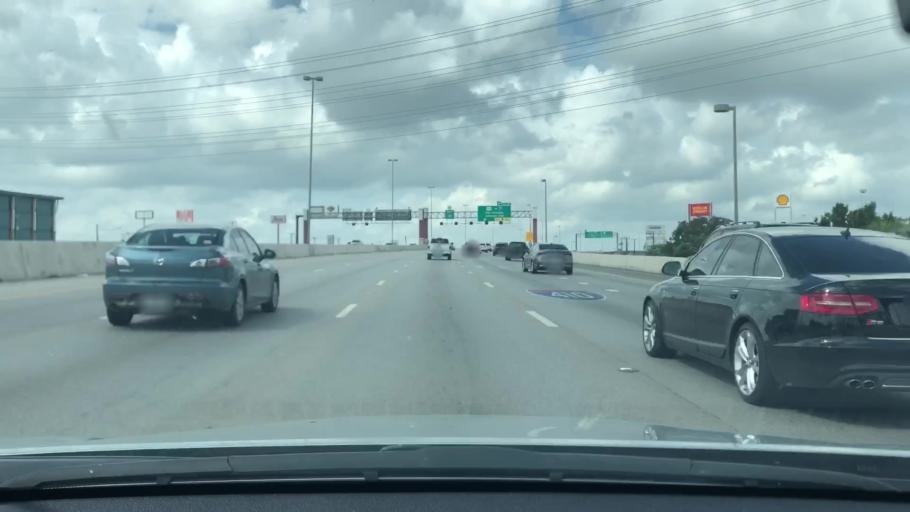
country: US
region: Texas
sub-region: Bexar County
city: Alamo Heights
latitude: 29.5173
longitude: -98.4628
